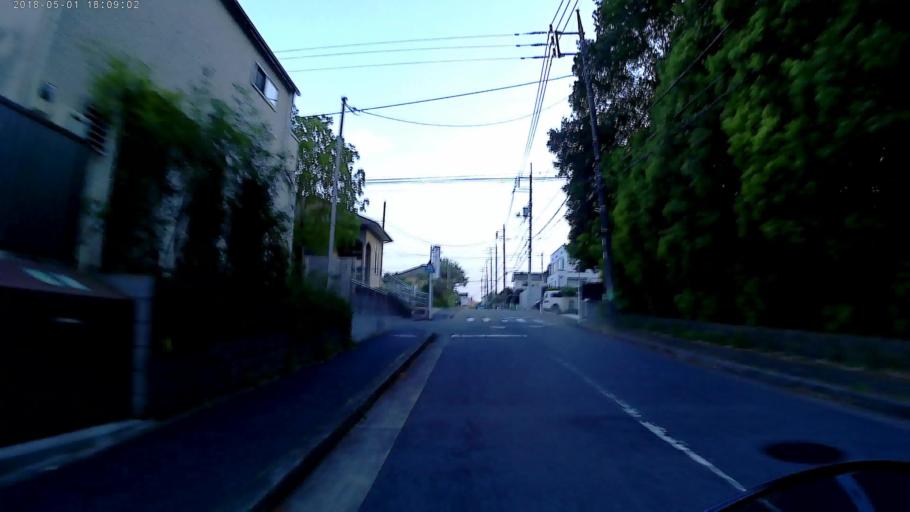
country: JP
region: Tokyo
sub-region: Machida-shi
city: Machida
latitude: 35.5416
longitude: 139.5600
